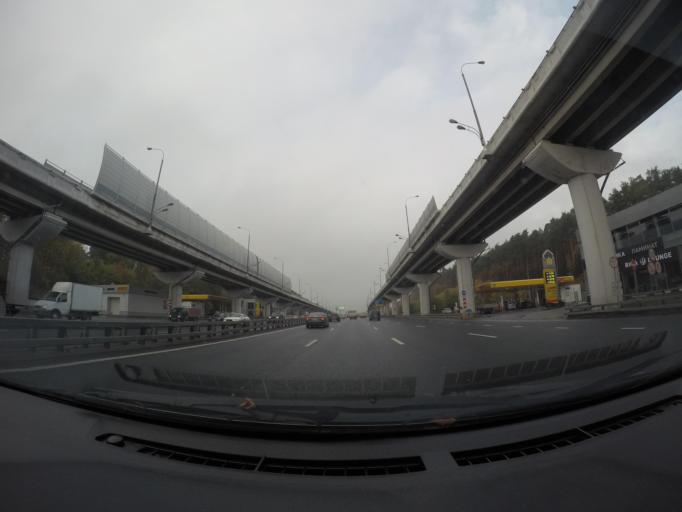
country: RU
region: Moscow
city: Rublevo
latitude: 55.7910
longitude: 37.3662
